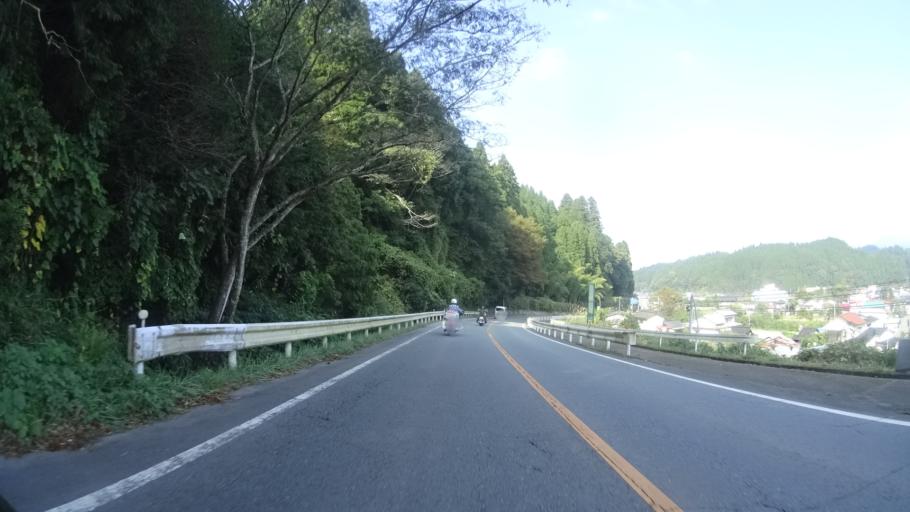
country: JP
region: Kumamoto
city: Aso
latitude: 33.0945
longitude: 131.0663
